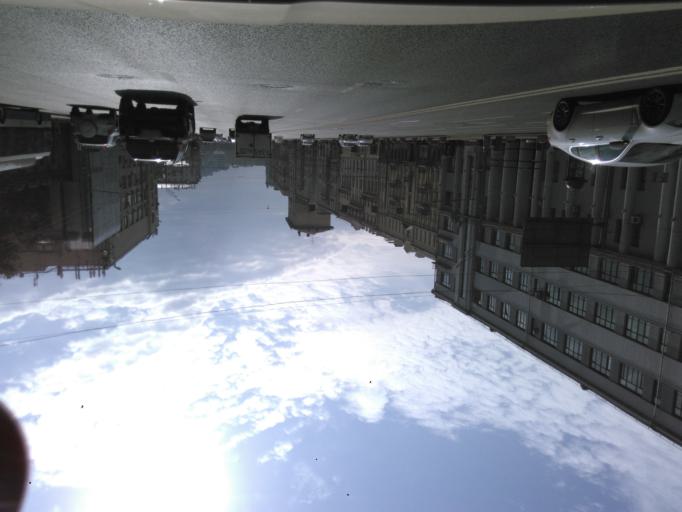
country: RU
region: Moscow
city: Moscow
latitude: 55.7683
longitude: 37.6501
